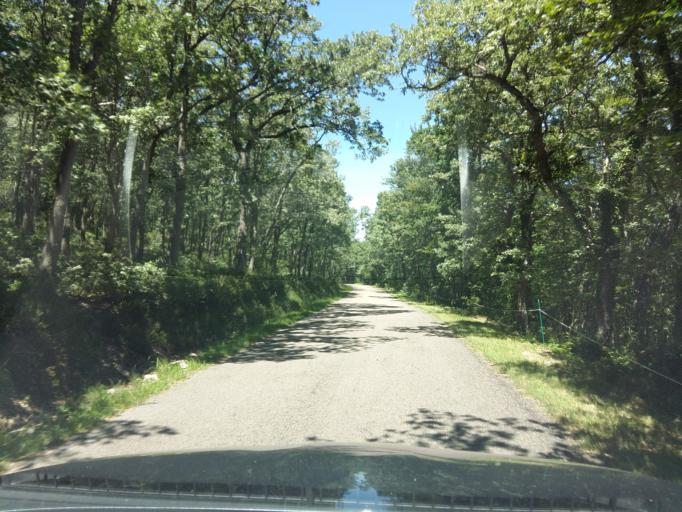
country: ES
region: Castille and Leon
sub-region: Provincia de Soria
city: Vozmediano
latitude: 41.8062
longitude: -1.8153
